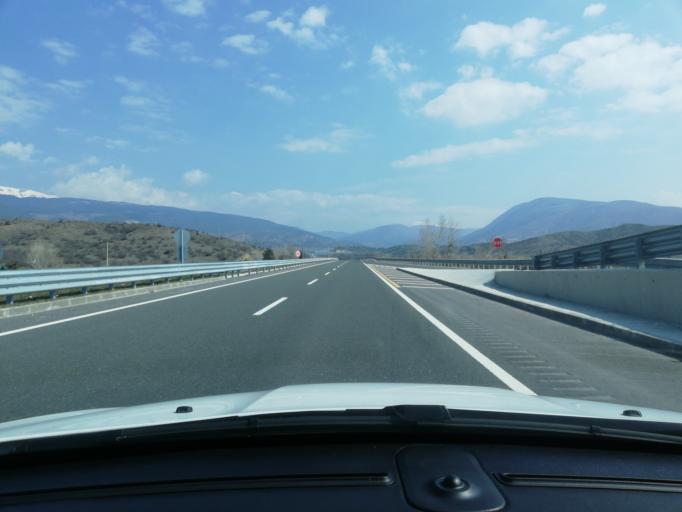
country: TR
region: Cankiri
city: Ilgaz
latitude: 40.9286
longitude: 33.6501
